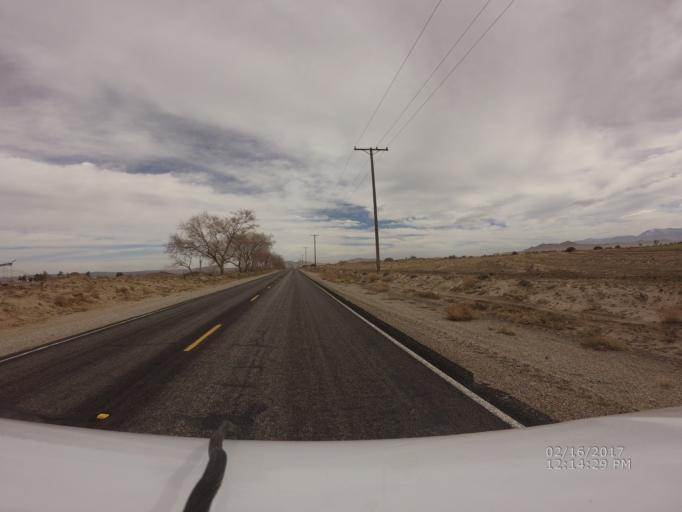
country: US
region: California
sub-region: Los Angeles County
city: Lake Los Angeles
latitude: 34.6757
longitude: -117.9399
